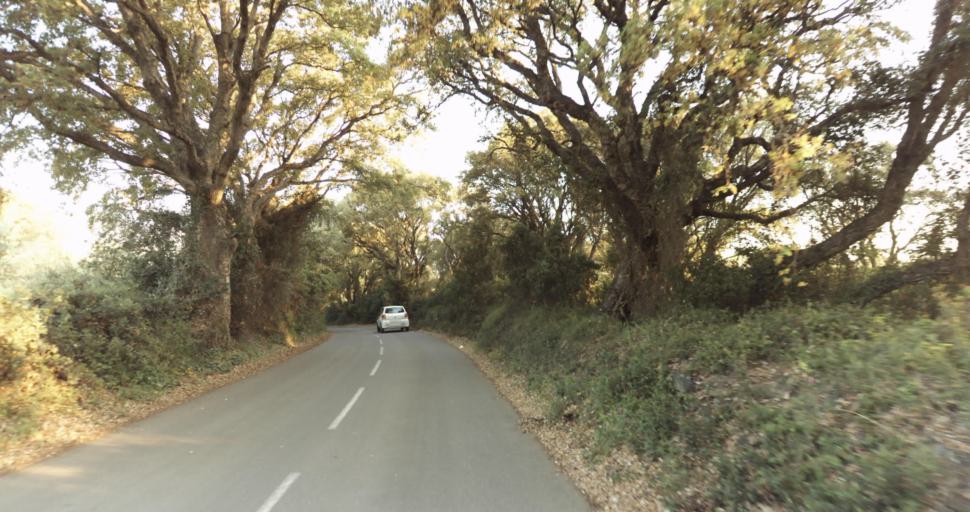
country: FR
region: Corsica
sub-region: Departement de la Haute-Corse
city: Biguglia
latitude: 42.6237
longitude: 9.4436
